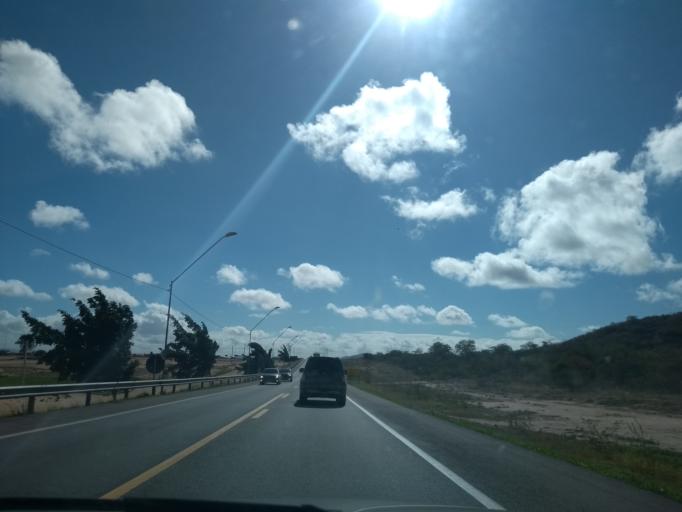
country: BR
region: Bahia
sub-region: Amargosa
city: Amargosa
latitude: -12.8631
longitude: -39.8528
